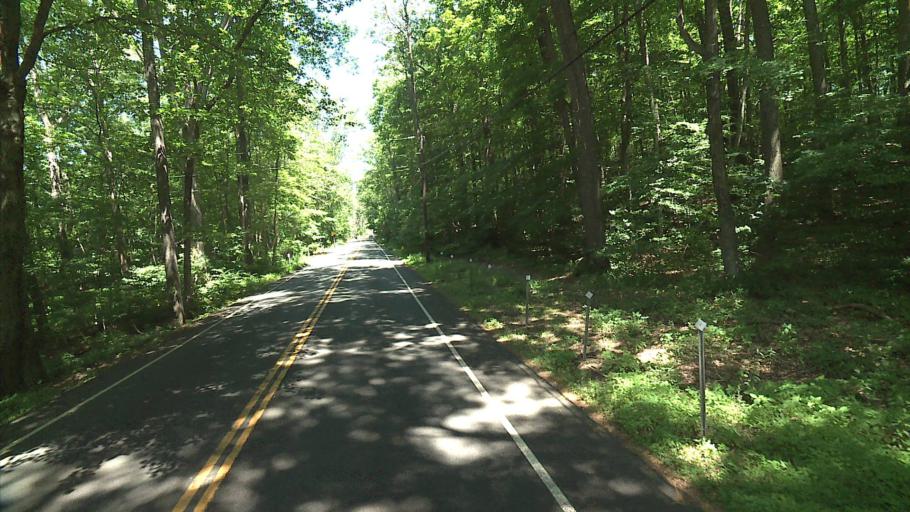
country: US
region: Connecticut
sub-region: New Haven County
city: North Branford
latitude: 41.3445
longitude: -72.7158
